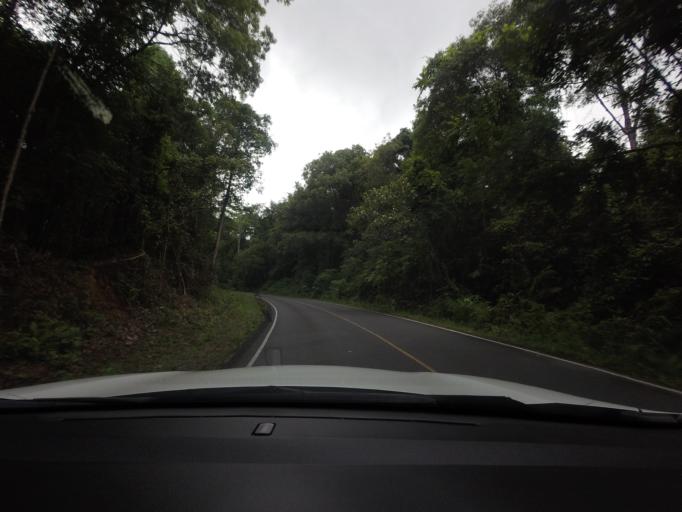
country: TH
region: Nakhon Nayok
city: Nakhon Nayok
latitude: 14.3575
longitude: 101.3457
